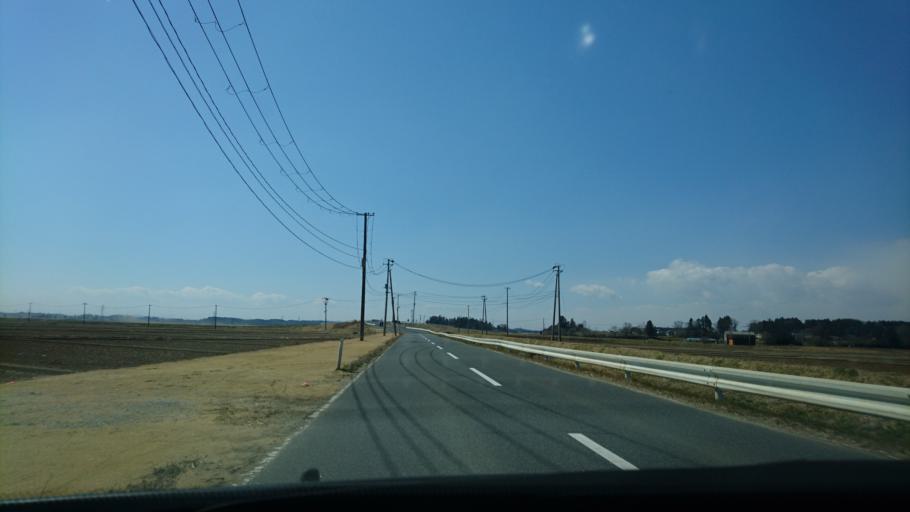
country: JP
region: Iwate
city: Ichinoseki
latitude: 38.7526
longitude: 141.1341
